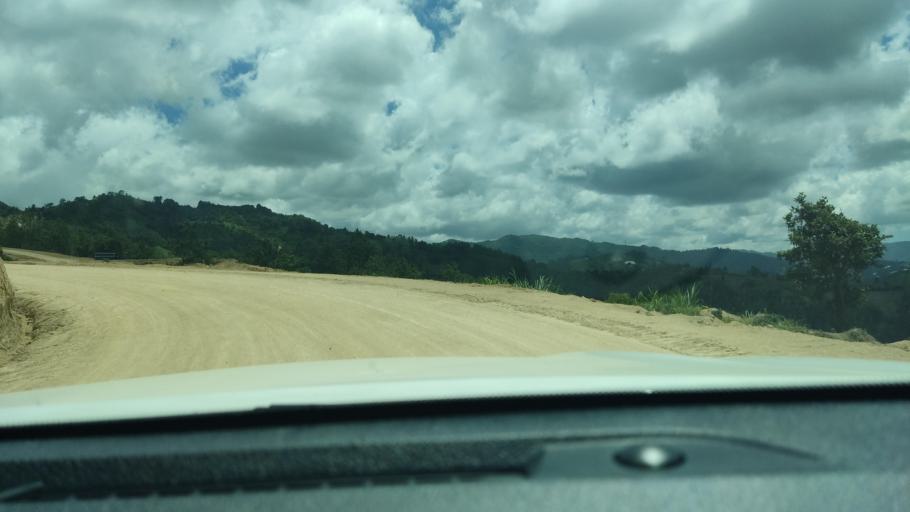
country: GT
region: Chimaltenango
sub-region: Municipio de San Juan Comalapa
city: Comalapa
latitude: 14.7853
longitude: -90.8654
